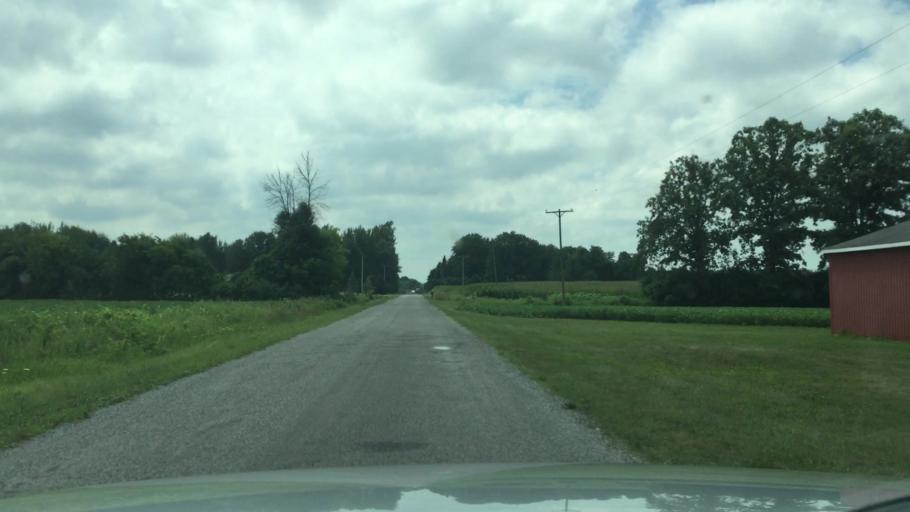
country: US
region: Michigan
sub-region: Saginaw County
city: Birch Run
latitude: 43.2987
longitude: -83.8347
